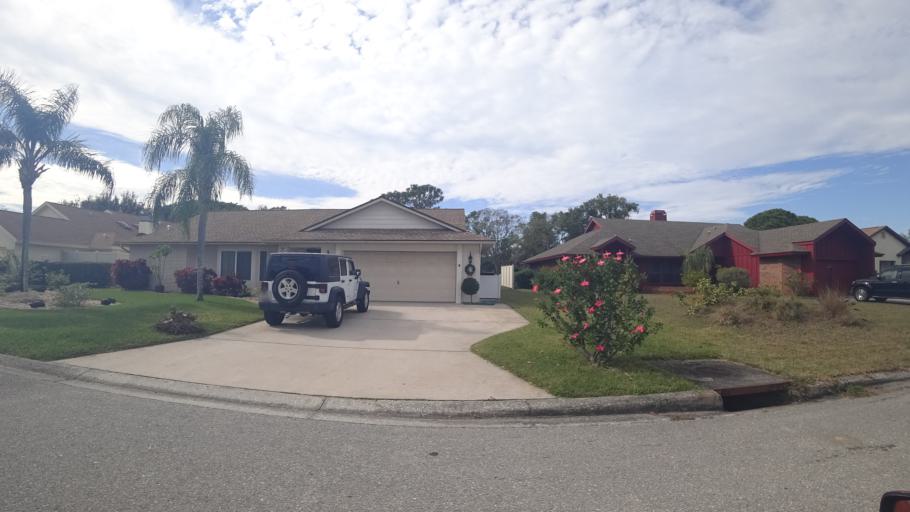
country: US
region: Florida
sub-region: Manatee County
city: West Bradenton
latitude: 27.5078
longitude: -82.6430
